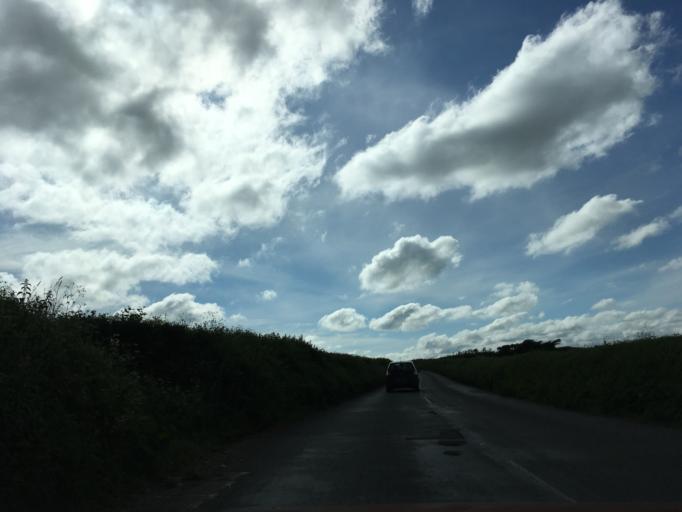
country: GB
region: England
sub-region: Devon
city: Totnes
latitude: 50.3658
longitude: -3.7073
